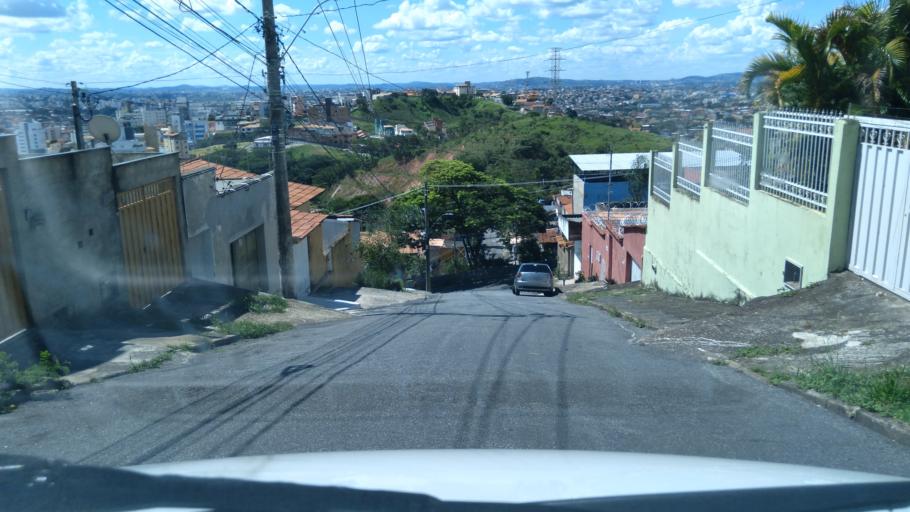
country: BR
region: Minas Gerais
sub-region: Belo Horizonte
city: Belo Horizonte
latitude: -19.8749
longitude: -43.9121
